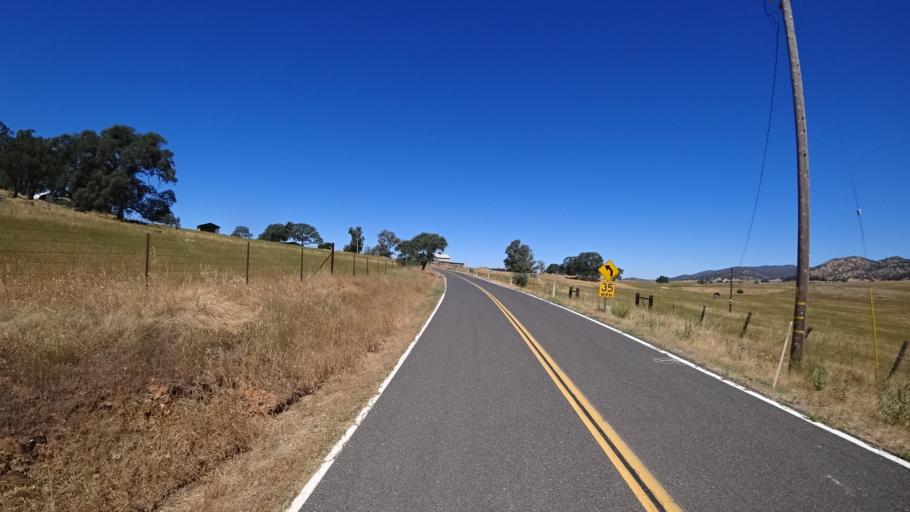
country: US
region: California
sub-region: Calaveras County
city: Copperopolis
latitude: 38.0243
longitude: -120.6895
